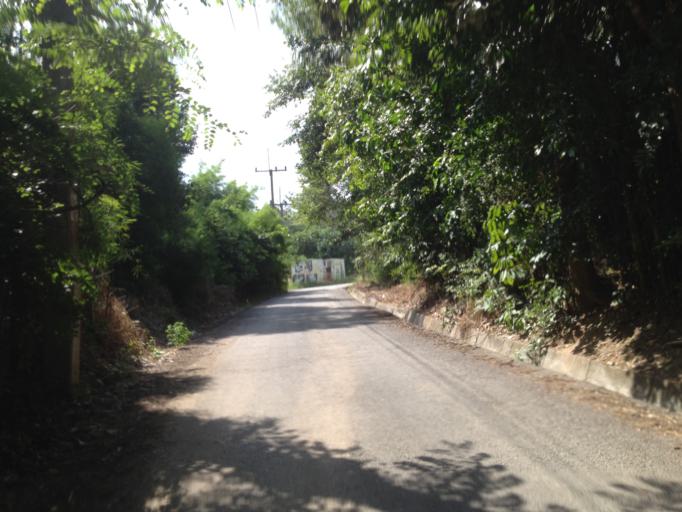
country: TH
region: Chiang Mai
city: Hang Dong
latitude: 18.7388
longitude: 98.9248
